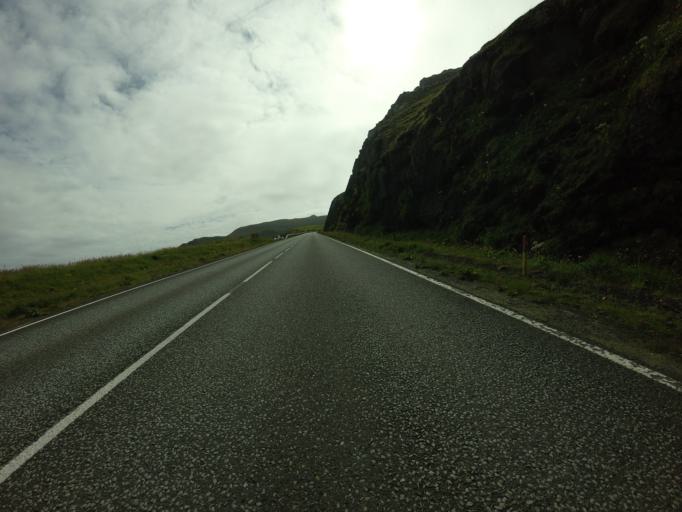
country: FO
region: Sandoy
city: Sandur
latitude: 61.9009
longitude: -6.8769
